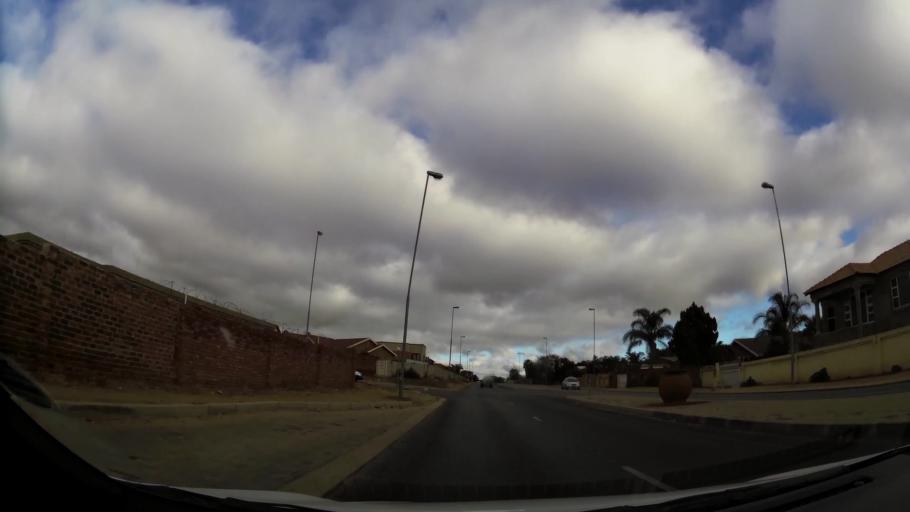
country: ZA
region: Limpopo
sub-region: Capricorn District Municipality
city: Polokwane
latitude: -23.9205
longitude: 29.4424
